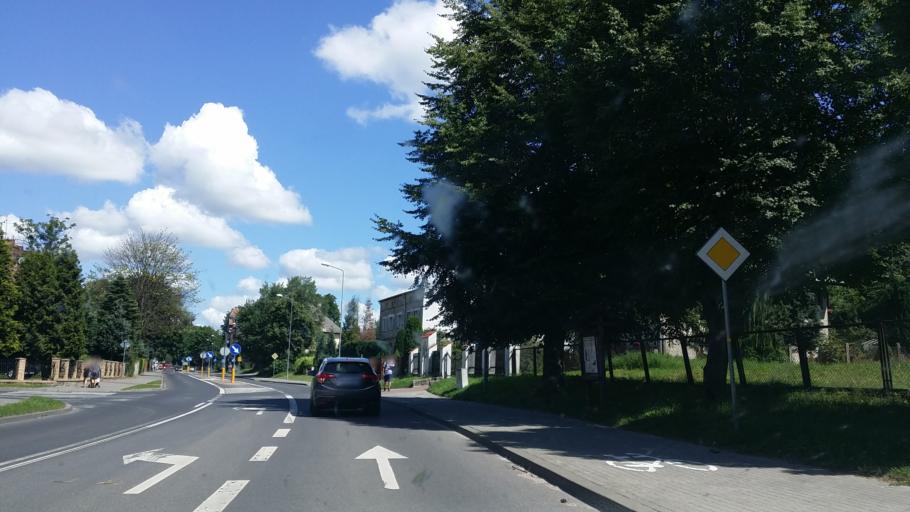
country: PL
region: West Pomeranian Voivodeship
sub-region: Powiat swidwinski
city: Swidwin
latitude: 53.7669
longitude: 15.7735
